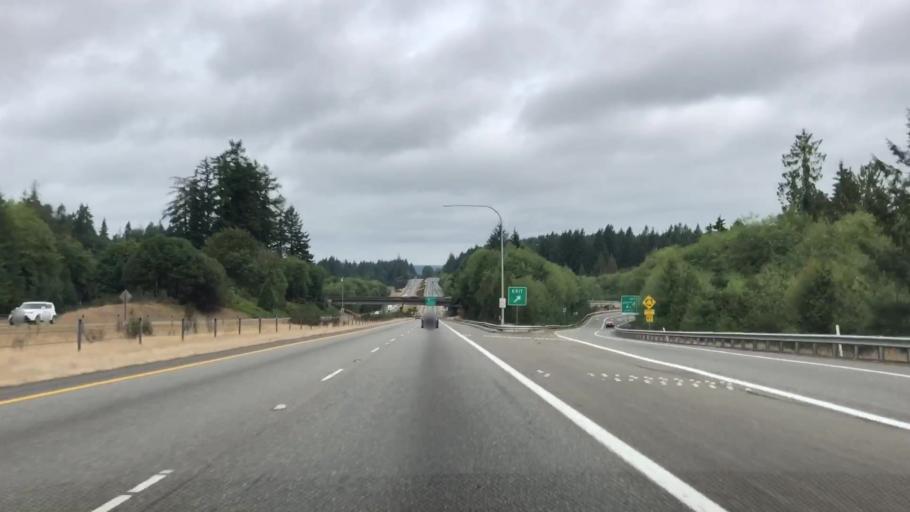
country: US
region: Washington
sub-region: Pierce County
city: Canterwood
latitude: 47.3555
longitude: -122.6130
